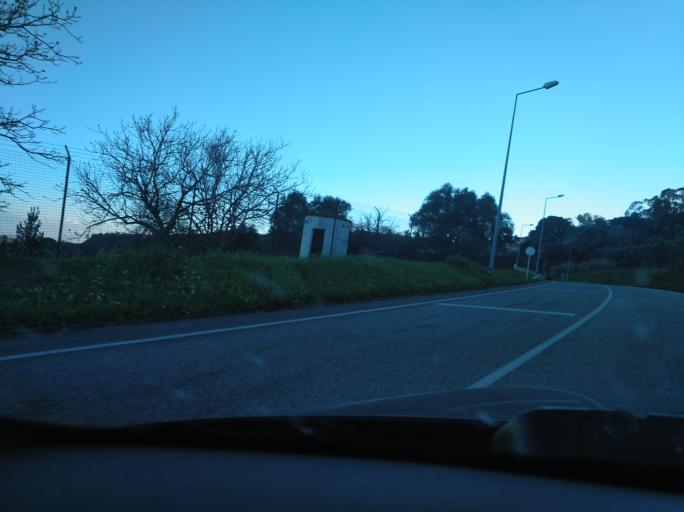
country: PT
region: Lisbon
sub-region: Loures
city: Unhos
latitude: 38.8276
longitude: -9.1262
